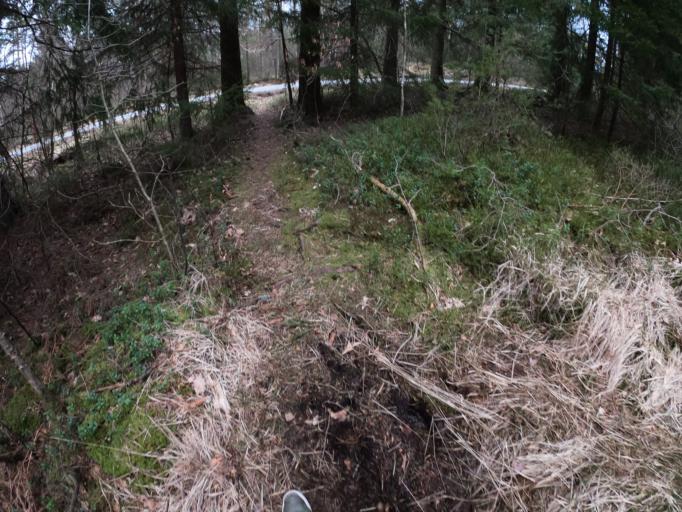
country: SE
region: Vaestra Goetaland
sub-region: Harryda Kommun
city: Molnlycke
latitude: 57.6404
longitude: 12.1085
